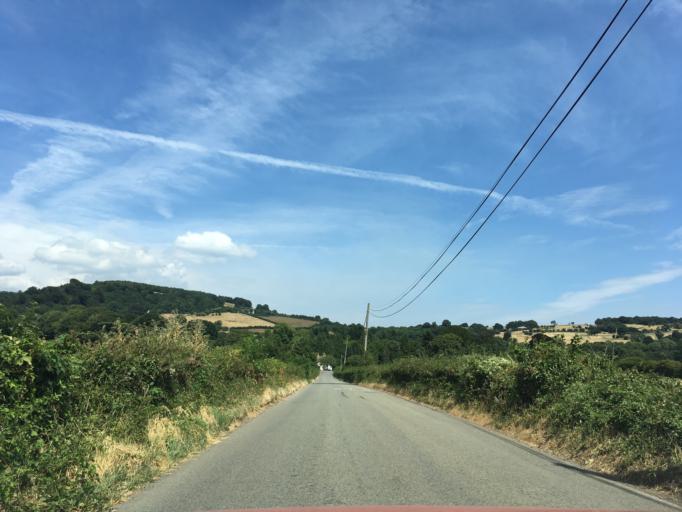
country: GB
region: Wales
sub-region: Caerphilly County Borough
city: Machen
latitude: 51.5832
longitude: -3.1213
